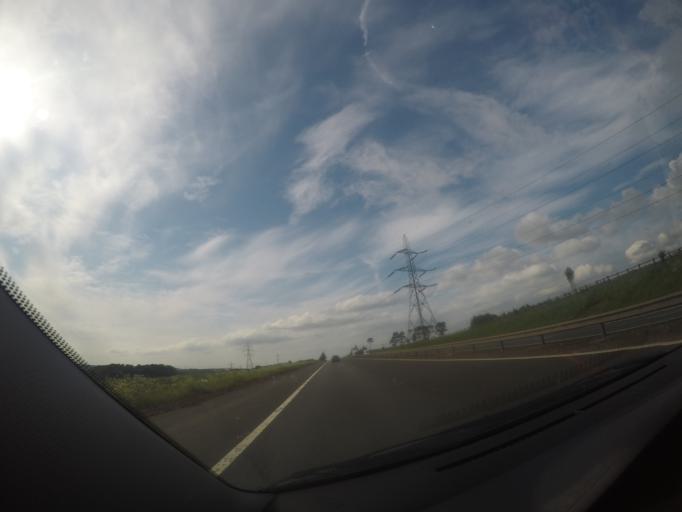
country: GB
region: Scotland
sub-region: South Lanarkshire
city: Lesmahagow
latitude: 55.6086
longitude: -3.8436
